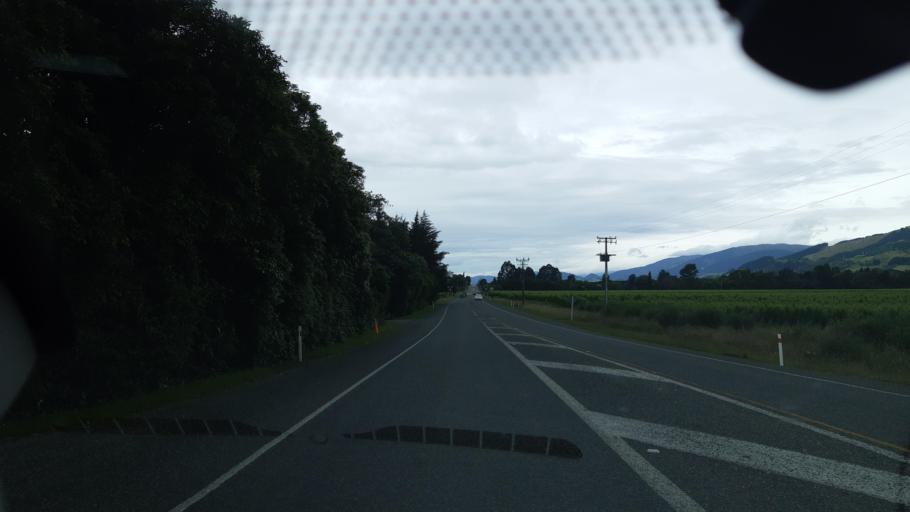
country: NZ
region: Tasman
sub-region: Tasman District
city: Brightwater
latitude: -41.3750
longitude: 173.1205
